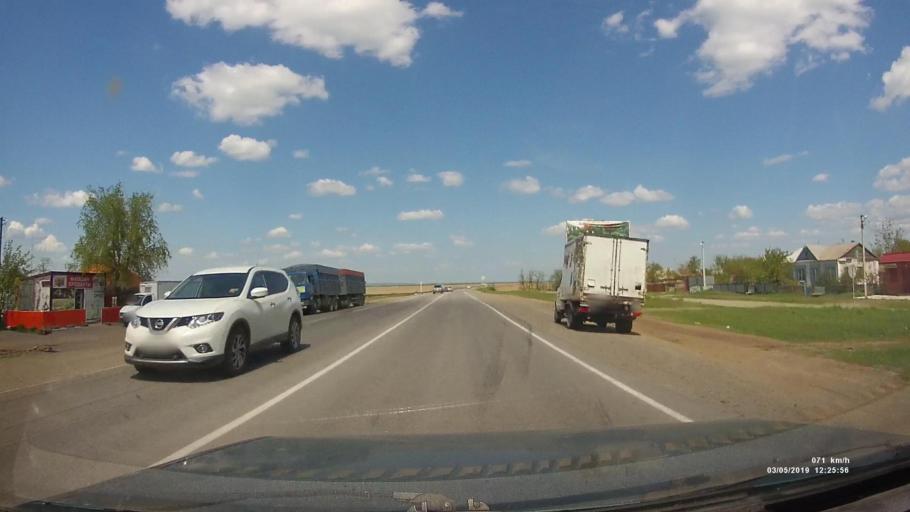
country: RU
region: Rostov
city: Semikarakorsk
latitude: 47.4389
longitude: 40.7119
